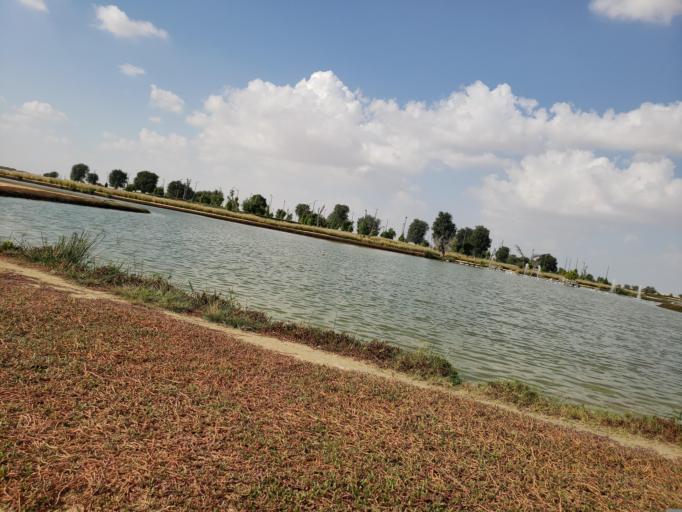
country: AE
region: Dubai
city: Dubai
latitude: 24.8549
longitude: 55.2504
